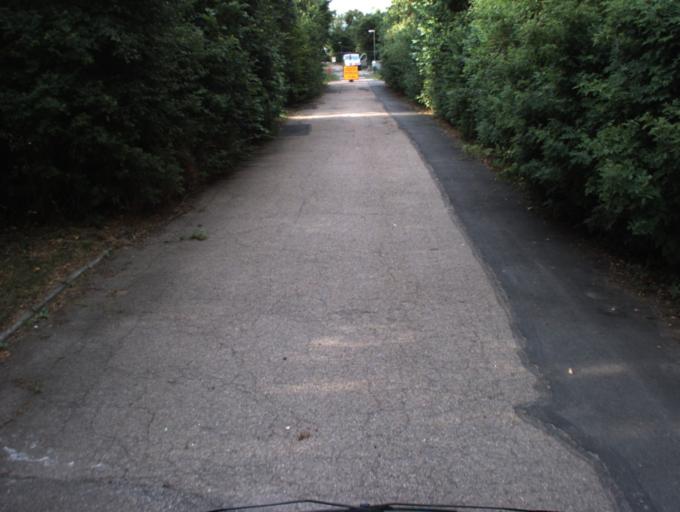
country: SE
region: Skane
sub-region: Helsingborg
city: Barslov
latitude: 56.0332
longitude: 12.8190
